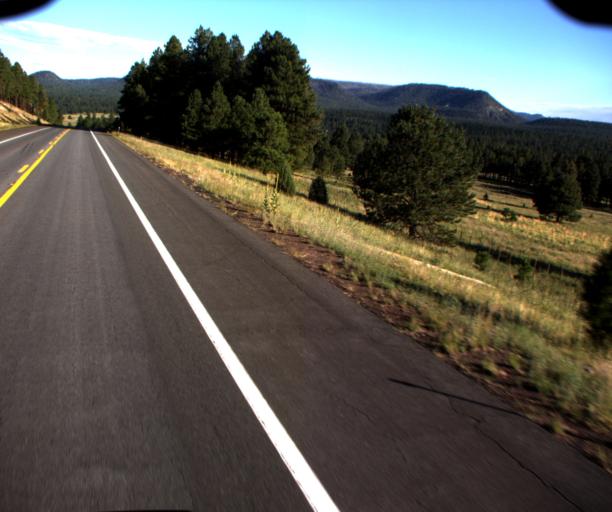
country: US
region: New Mexico
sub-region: Catron County
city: Reserve
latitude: 33.8222
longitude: -109.0775
